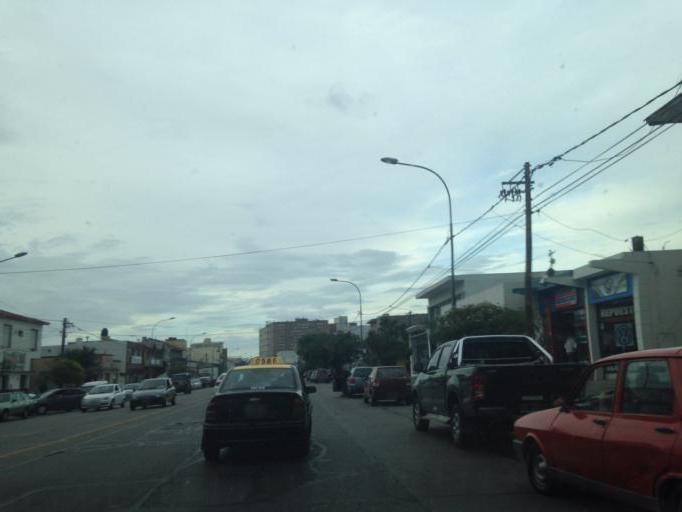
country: AR
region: Buenos Aires
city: Mar del Plata
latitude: -38.0216
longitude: -57.5743
